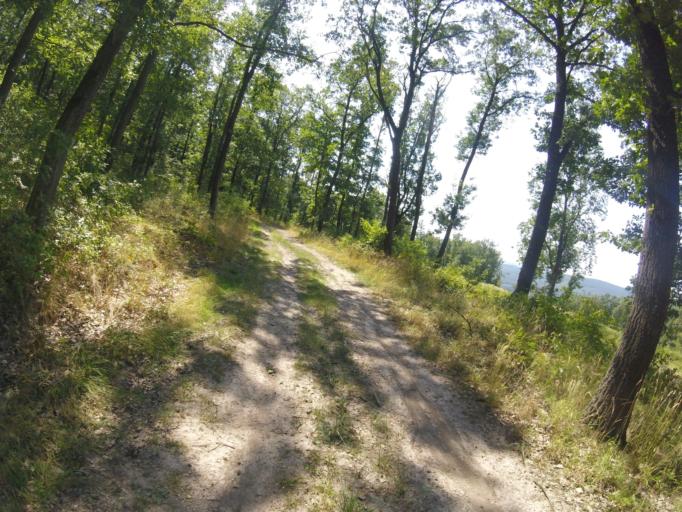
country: HU
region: Pest
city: Csobanka
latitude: 47.6818
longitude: 18.9601
